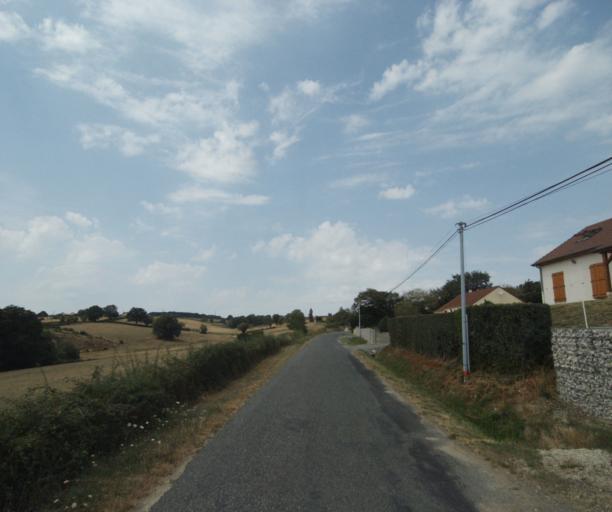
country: FR
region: Bourgogne
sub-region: Departement de Saone-et-Loire
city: Gueugnon
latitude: 46.6004
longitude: 4.0128
